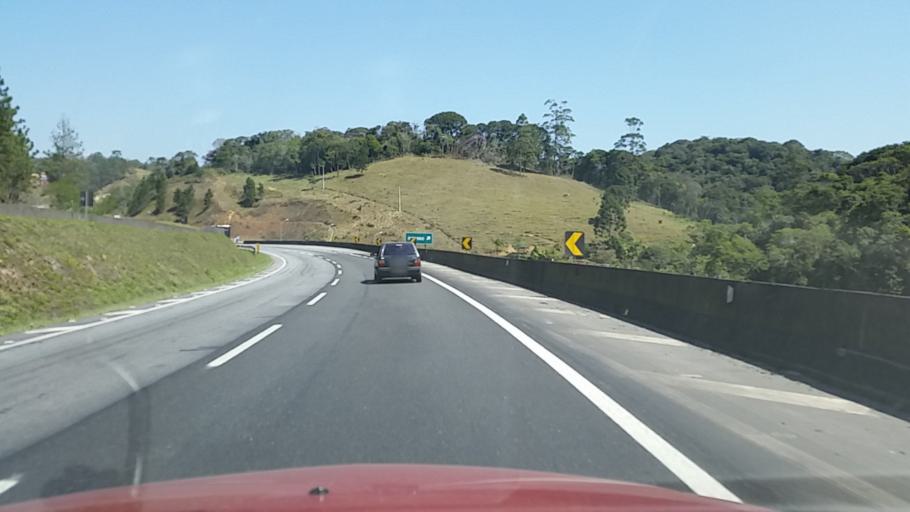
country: BR
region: Sao Paulo
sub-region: Juquitiba
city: Juquitiba
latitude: -24.0036
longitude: -47.1577
